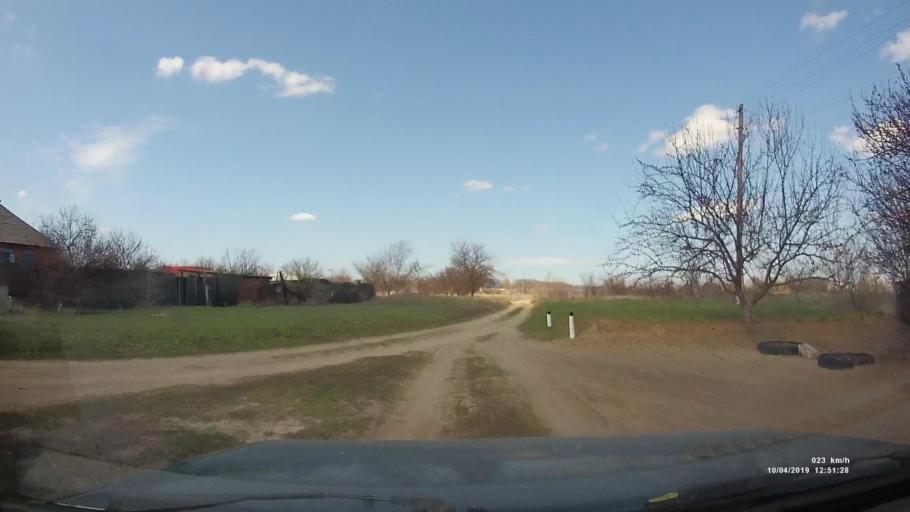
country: RU
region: Rostov
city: Kamensk-Shakhtinskiy
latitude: 48.3595
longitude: 40.2171
